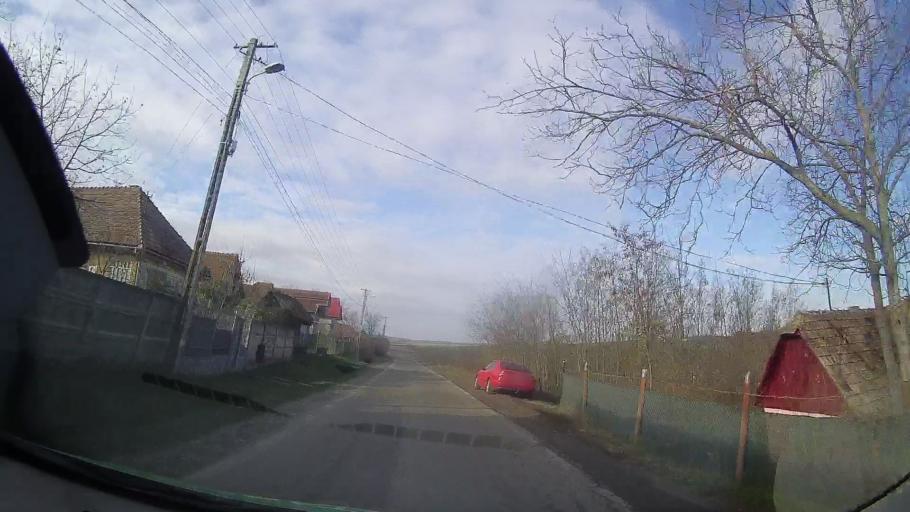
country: RO
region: Mures
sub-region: Comuna Sanger
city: Sanger
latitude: 46.5558
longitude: 24.1411
